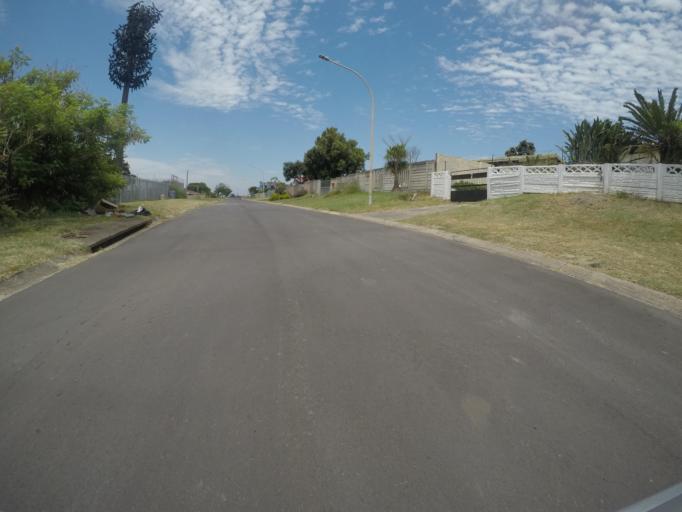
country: ZA
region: Eastern Cape
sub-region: Buffalo City Metropolitan Municipality
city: East London
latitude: -32.9812
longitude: 27.8656
